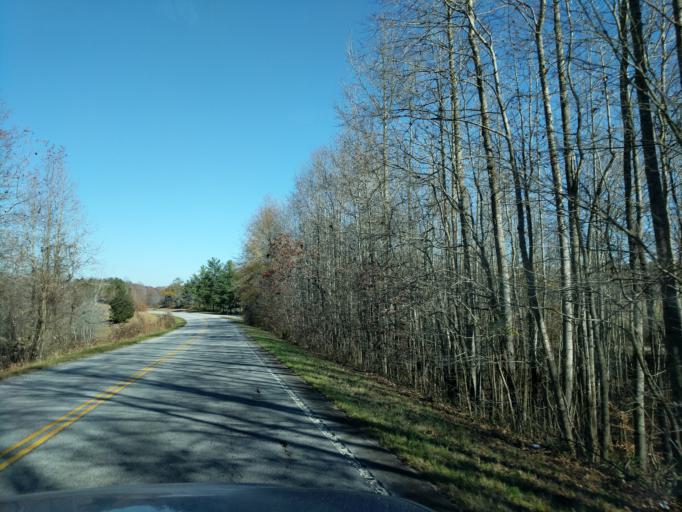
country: US
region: South Carolina
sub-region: Spartanburg County
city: Landrum
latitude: 35.1253
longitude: -82.2238
